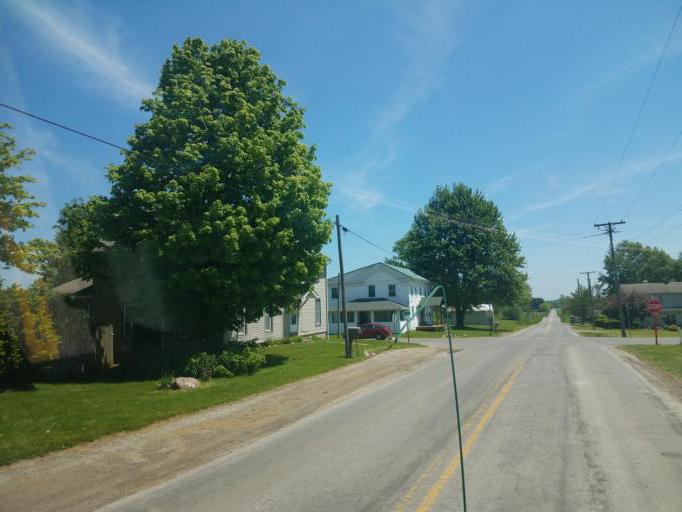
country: US
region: Ohio
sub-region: Wayne County
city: West Salem
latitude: 40.9741
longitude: -82.1634
